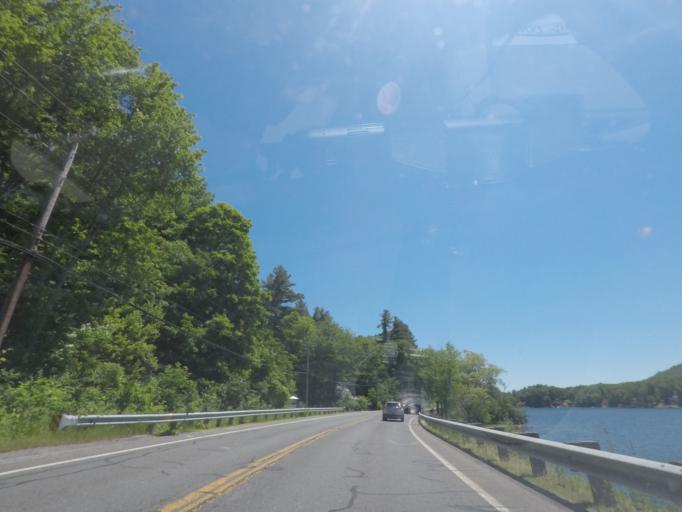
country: US
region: Massachusetts
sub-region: Berkshire County
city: Becket
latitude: 42.2865
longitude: -73.1475
